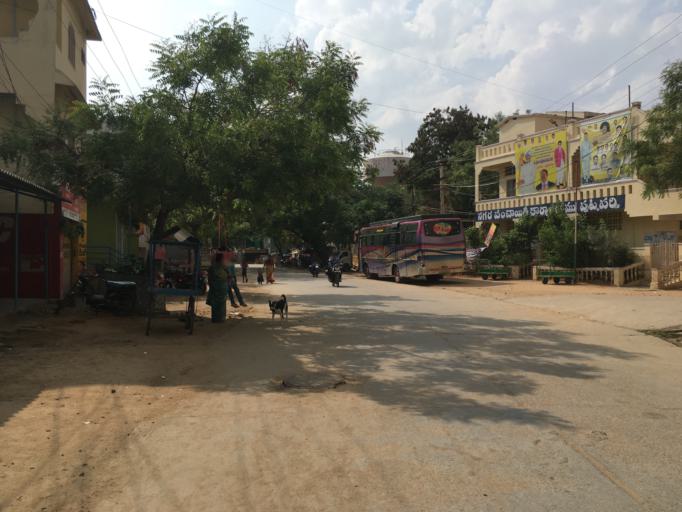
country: IN
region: Andhra Pradesh
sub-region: Anantapur
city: Puttaparthi
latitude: 14.1690
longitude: 77.8119
